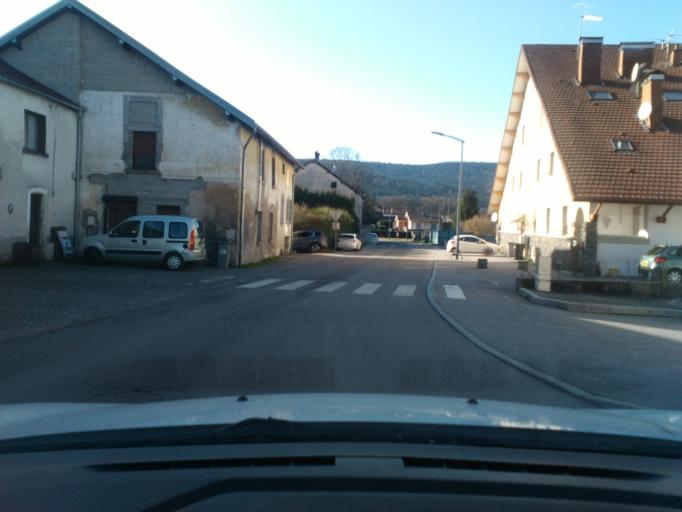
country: FR
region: Lorraine
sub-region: Departement des Vosges
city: Vecoux
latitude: 47.9803
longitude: 6.6364
